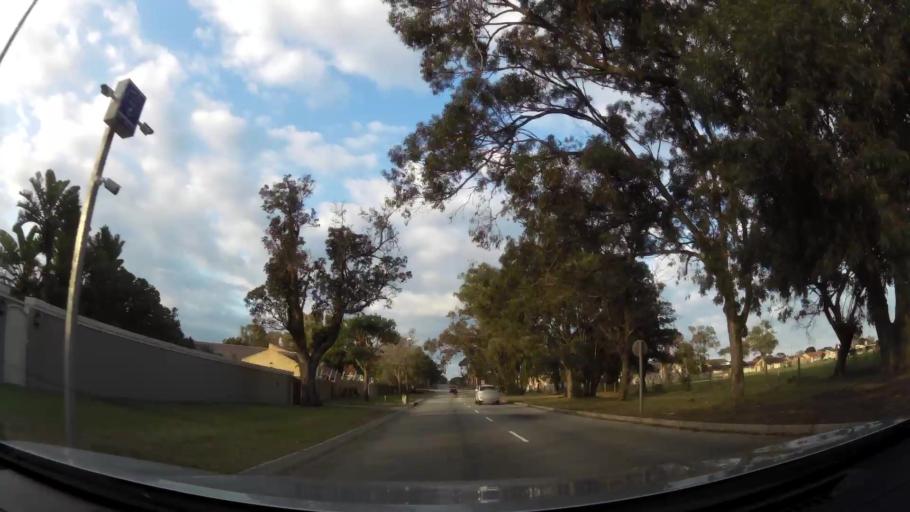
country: ZA
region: Eastern Cape
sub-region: Nelson Mandela Bay Metropolitan Municipality
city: Port Elizabeth
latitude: -33.9808
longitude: 25.5639
